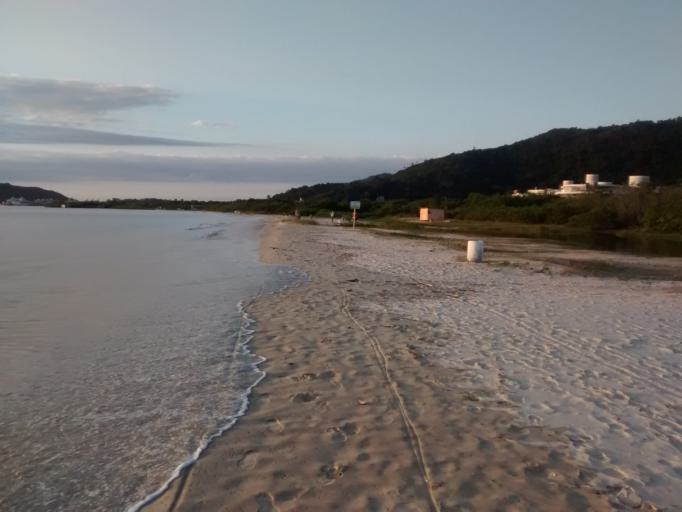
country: BR
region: Santa Catarina
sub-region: Florianopolis
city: Itacorubi
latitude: -27.4140
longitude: -48.4290
